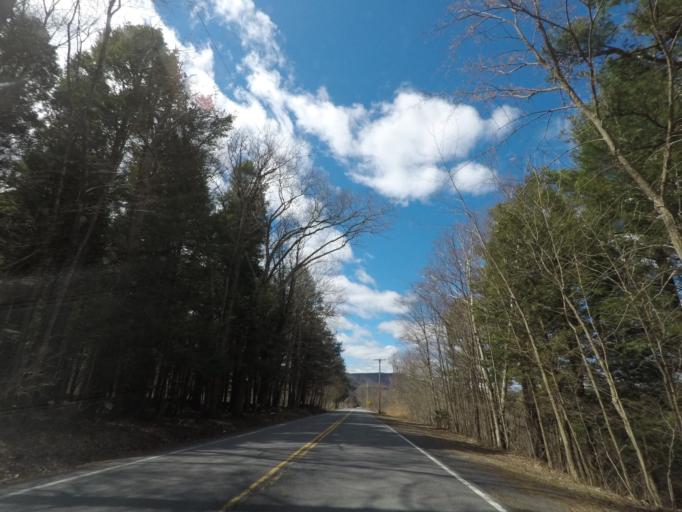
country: US
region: New York
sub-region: Albany County
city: Voorheesville
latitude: 42.6510
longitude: -73.9834
